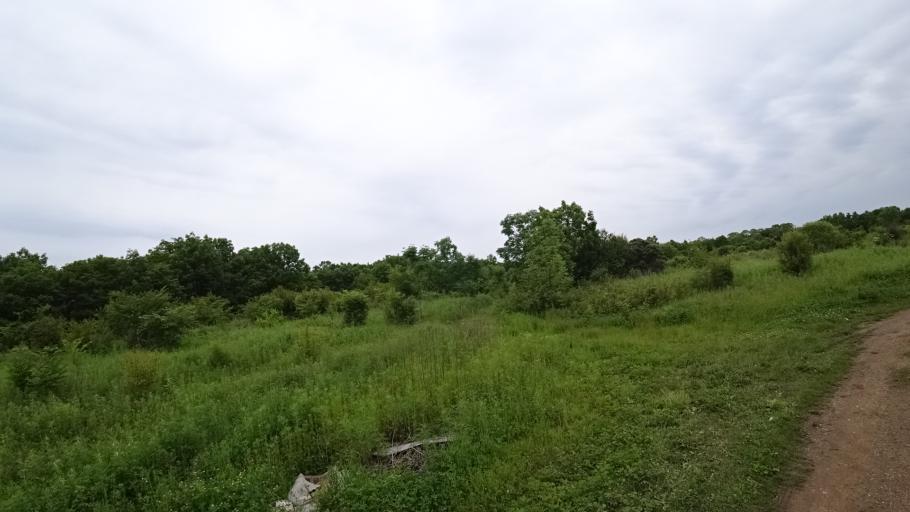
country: RU
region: Primorskiy
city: Novosysoyevka
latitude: 44.2113
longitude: 133.3265
